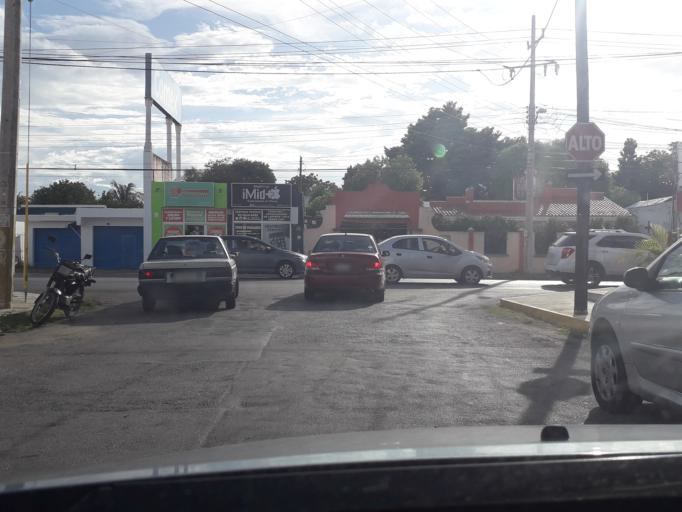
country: MX
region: Yucatan
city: Merida
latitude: 21.0023
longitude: -89.6388
